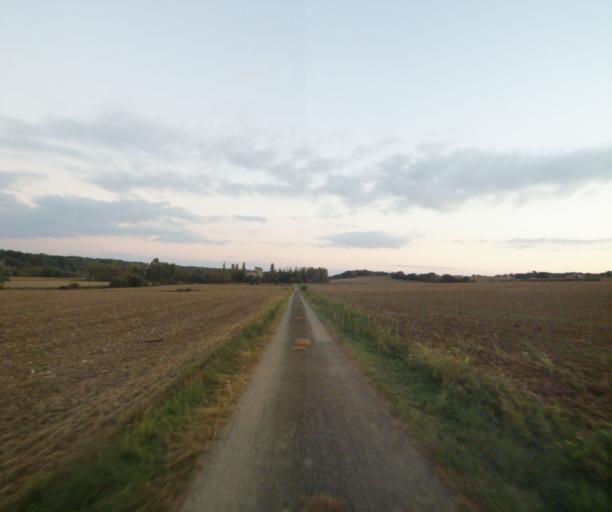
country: FR
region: Midi-Pyrenees
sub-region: Departement du Gers
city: Vic-Fezensac
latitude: 43.8126
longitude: 0.2532
